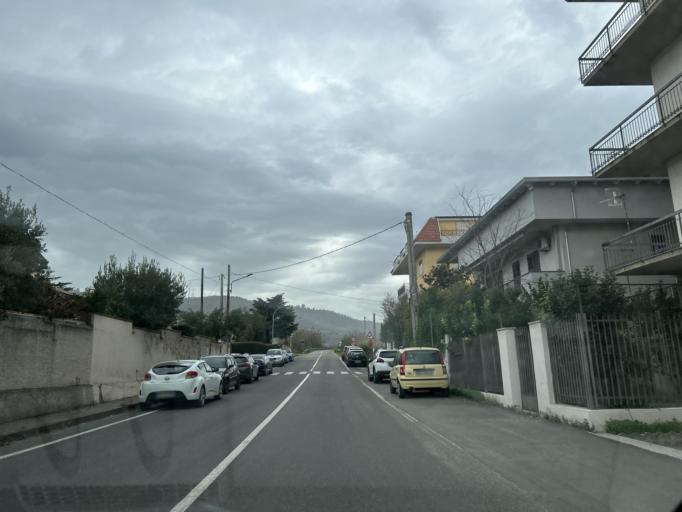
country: IT
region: Calabria
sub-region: Provincia di Catanzaro
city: Montepaone Lido
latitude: 38.7320
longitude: 16.5443
